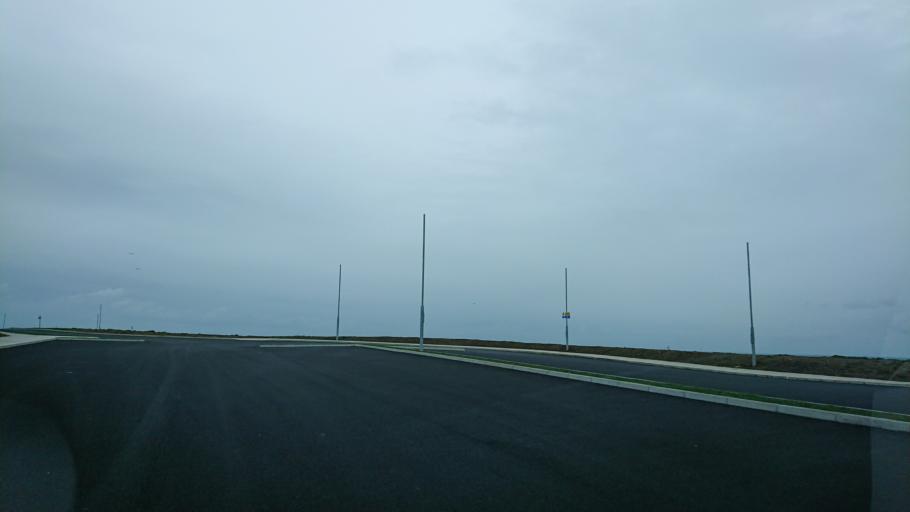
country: IE
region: Munster
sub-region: Waterford
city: Dunmore East
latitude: 52.1454
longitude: -6.9928
